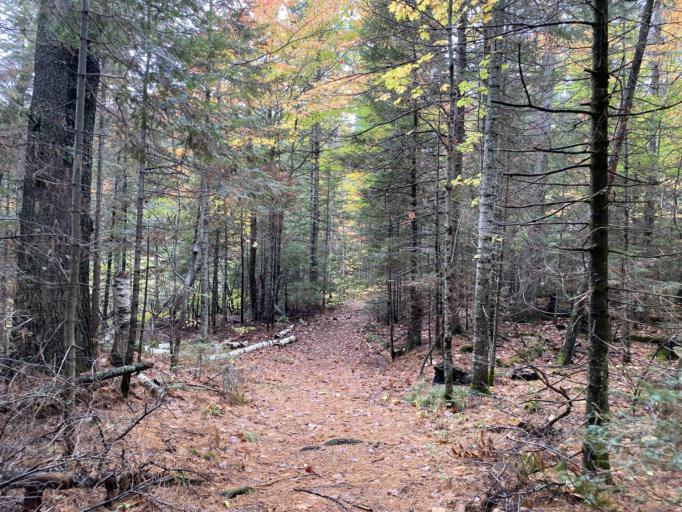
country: US
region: Michigan
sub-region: Marquette County
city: West Ishpeming
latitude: 46.5318
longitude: -88.0003
